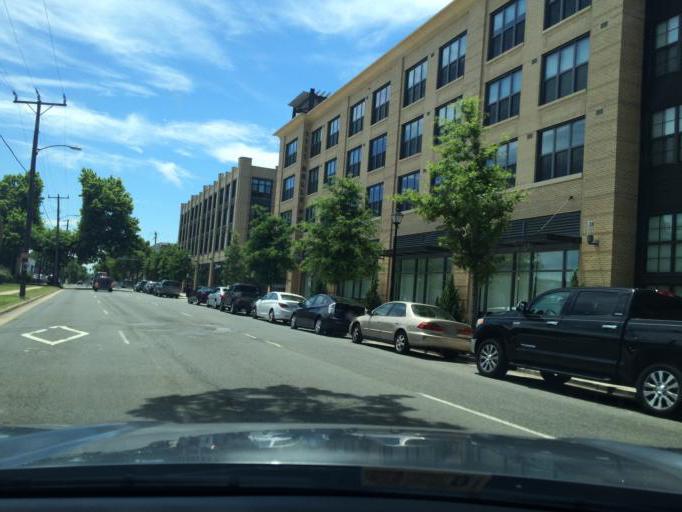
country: US
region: Virginia
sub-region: City of Alexandria
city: Alexandria
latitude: 38.8146
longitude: -77.0494
